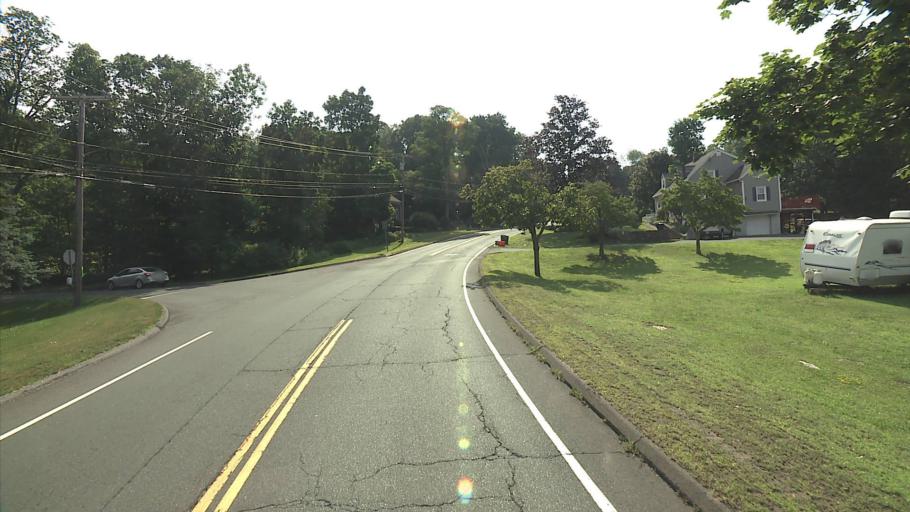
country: US
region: Connecticut
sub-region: New Haven County
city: Wolcott
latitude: 41.6053
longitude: -72.9837
